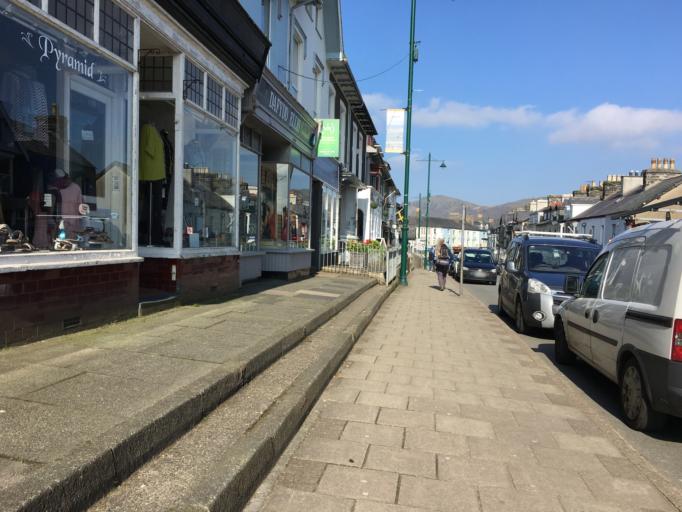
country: GB
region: Wales
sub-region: Gwynedd
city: Porthmadog
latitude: 52.9270
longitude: -4.1318
